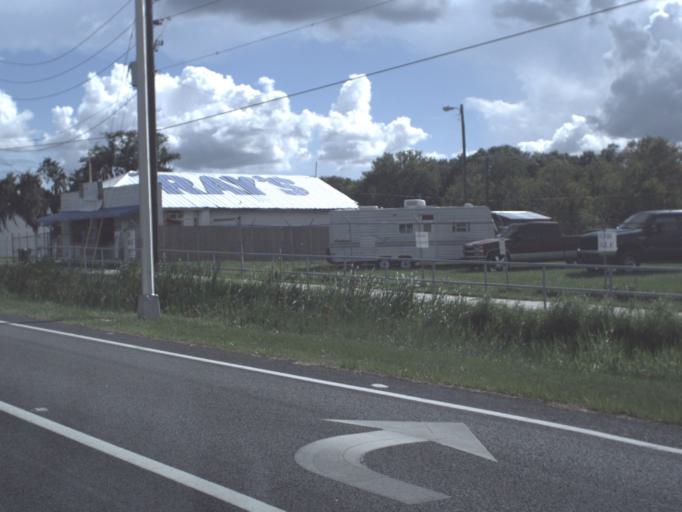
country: US
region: Florida
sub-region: Hillsborough County
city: Plant City
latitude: 27.9531
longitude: -82.1213
